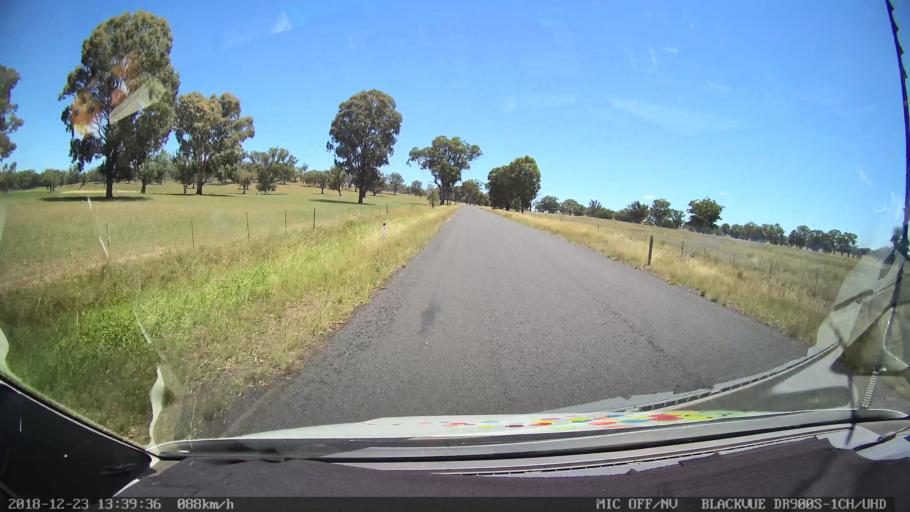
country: AU
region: New South Wales
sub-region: Armidale Dumaresq
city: Armidale
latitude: -30.4595
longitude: 151.1998
